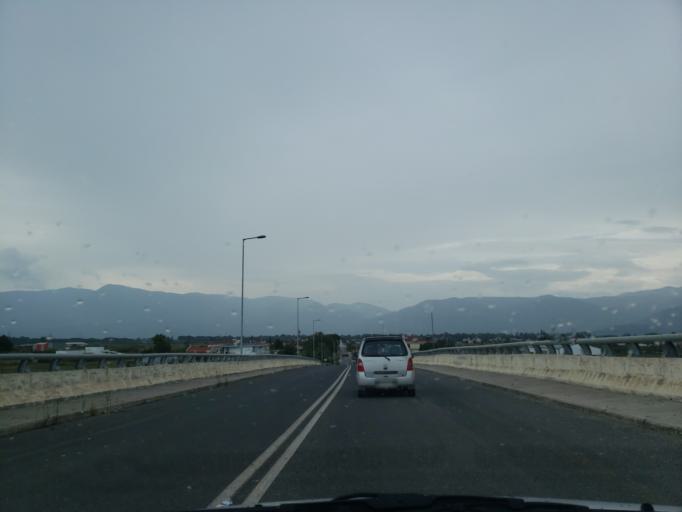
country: GR
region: Central Greece
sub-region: Nomos Fthiotidos
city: Rodhitsa
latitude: 38.8672
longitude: 22.4396
